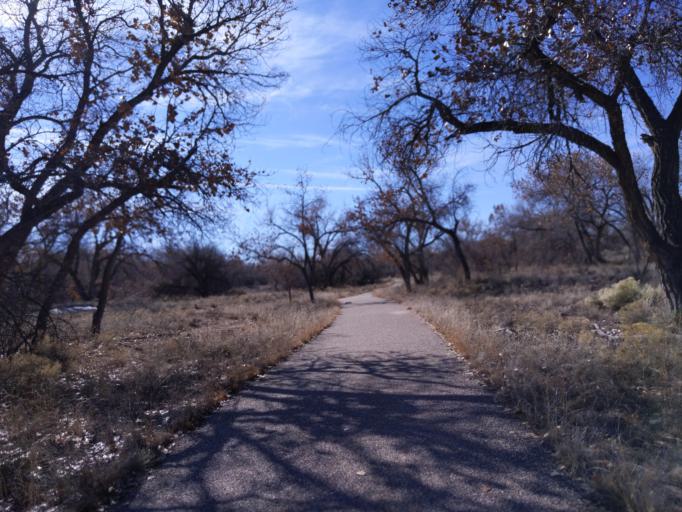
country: US
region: New Mexico
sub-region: Bernalillo County
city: Lee Acres
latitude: 35.1356
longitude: -106.6824
